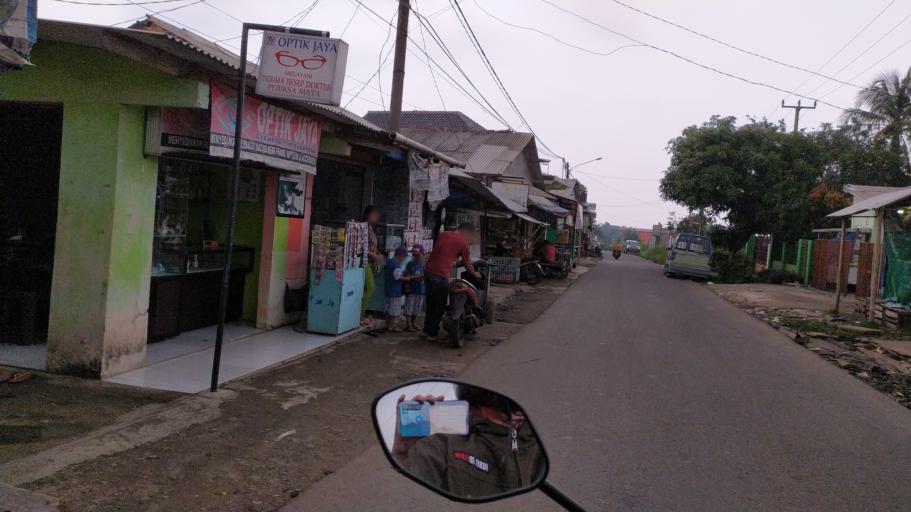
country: ID
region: West Java
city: Ciampea
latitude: -6.6174
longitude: 106.6951
